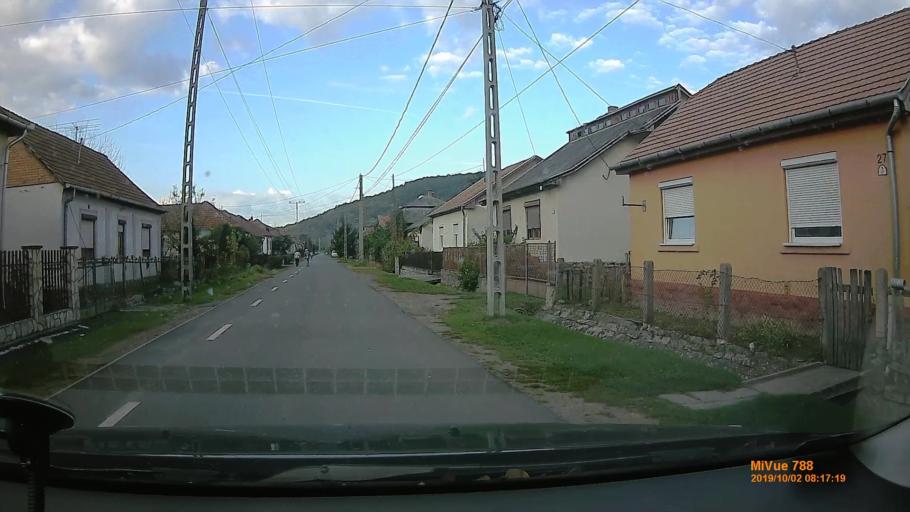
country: HU
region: Nograd
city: Matraverebely
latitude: 47.9726
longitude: 19.7752
